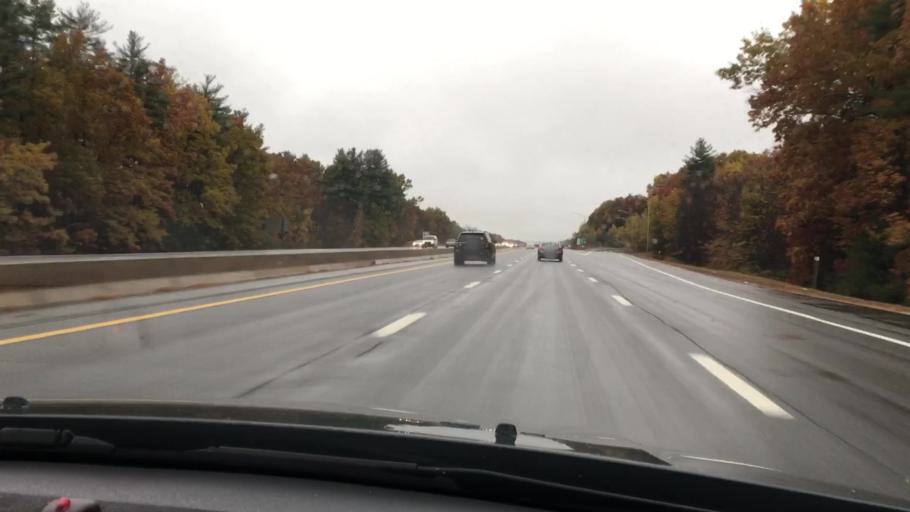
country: US
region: New Hampshire
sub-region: Hillsborough County
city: Litchfield
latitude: 42.8277
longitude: -71.4945
